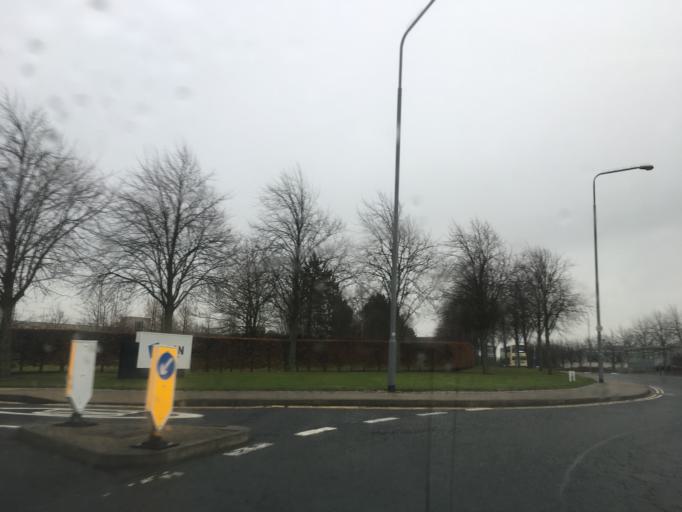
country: GB
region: Scotland
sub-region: Edinburgh
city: Currie
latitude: 55.9338
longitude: -3.3156
